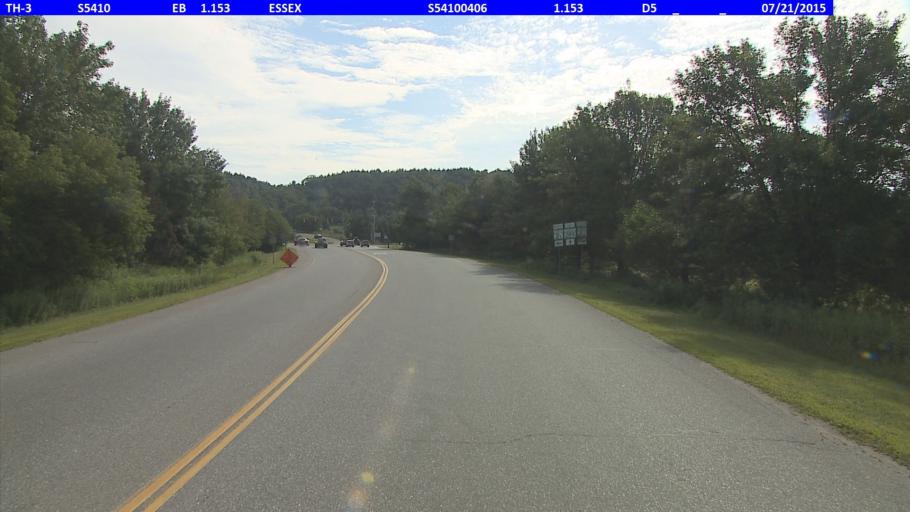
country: US
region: Vermont
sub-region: Chittenden County
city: Essex Junction
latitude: 44.5149
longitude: -73.1244
